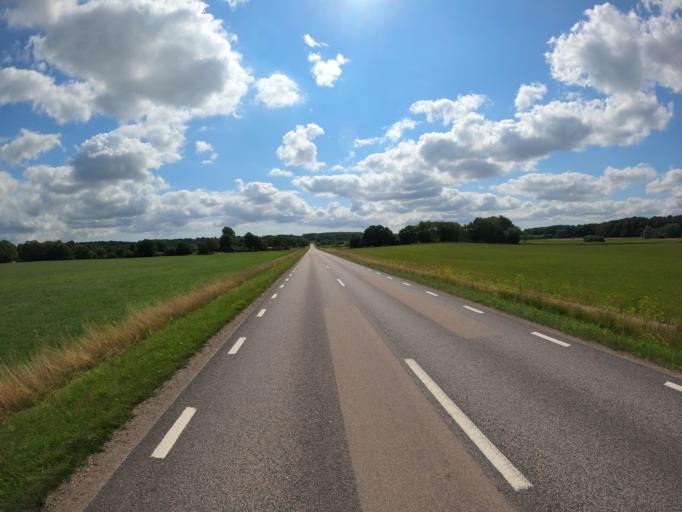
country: SE
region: Skane
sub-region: Lunds Kommun
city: Veberod
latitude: 55.6000
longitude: 13.4903
